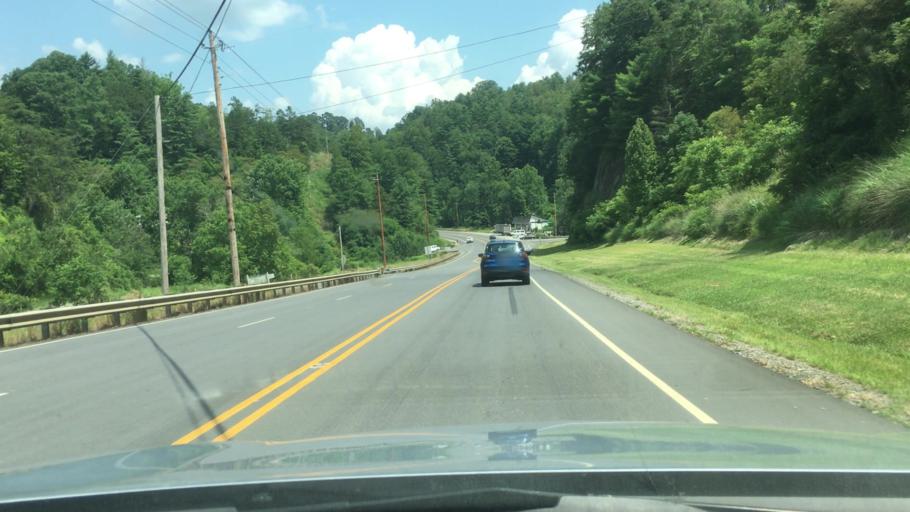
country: US
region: North Carolina
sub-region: Madison County
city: Mars Hill
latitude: 35.8241
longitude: -82.6141
